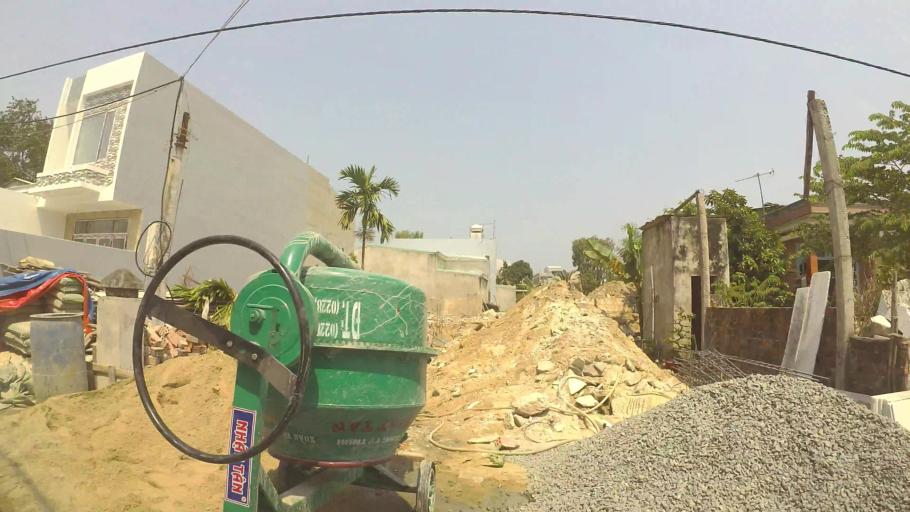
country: VN
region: Da Nang
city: Ngu Hanh Son
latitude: 15.9935
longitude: 108.2636
